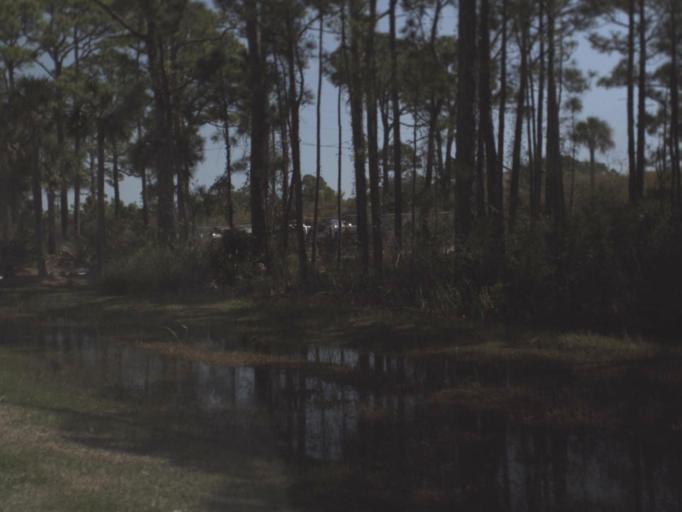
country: US
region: Florida
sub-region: Gulf County
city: Port Saint Joe
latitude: 29.6831
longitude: -85.3285
